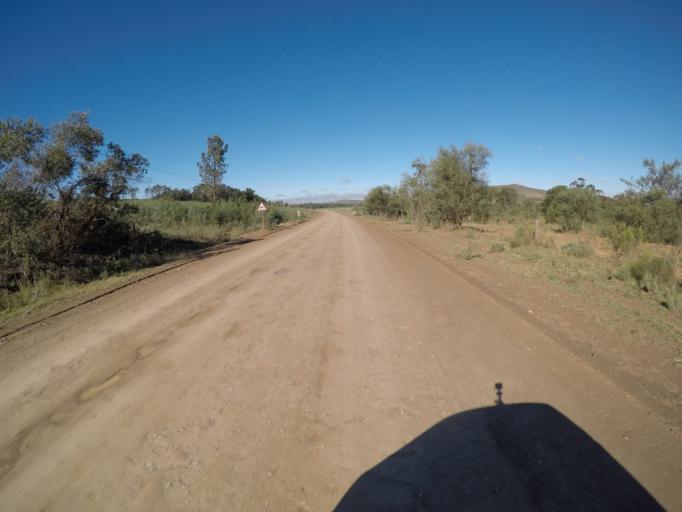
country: ZA
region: Western Cape
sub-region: Overberg District Municipality
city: Caledon
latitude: -34.0670
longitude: 19.6296
